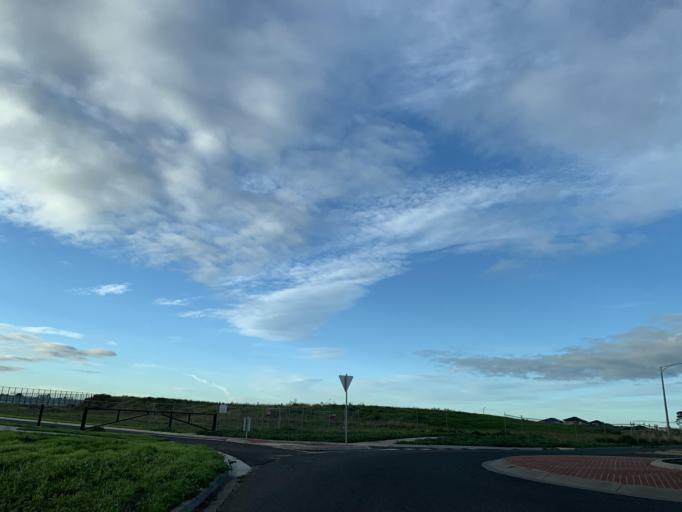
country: AU
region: Victoria
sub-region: Casey
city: Cranbourne East
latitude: -38.1248
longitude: 145.3068
